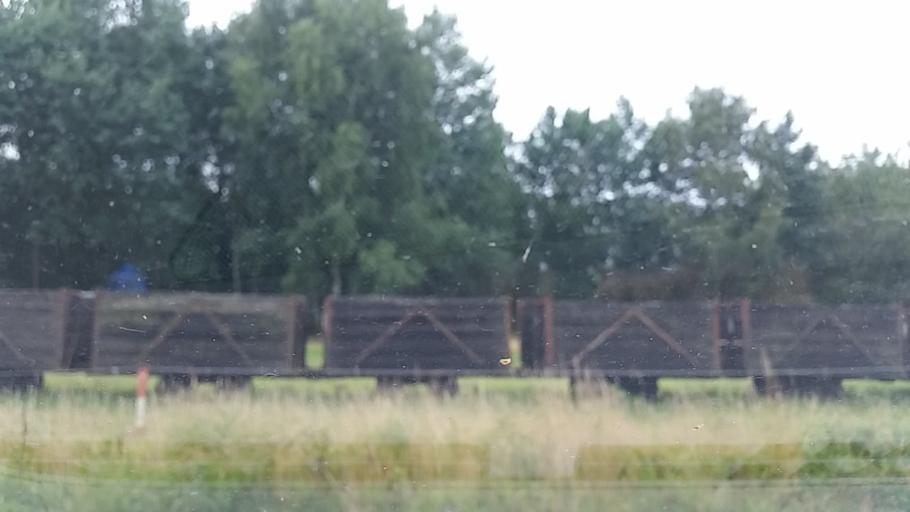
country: DE
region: Schleswig-Holstein
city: Bilsen
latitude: 53.7413
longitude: 9.8719
